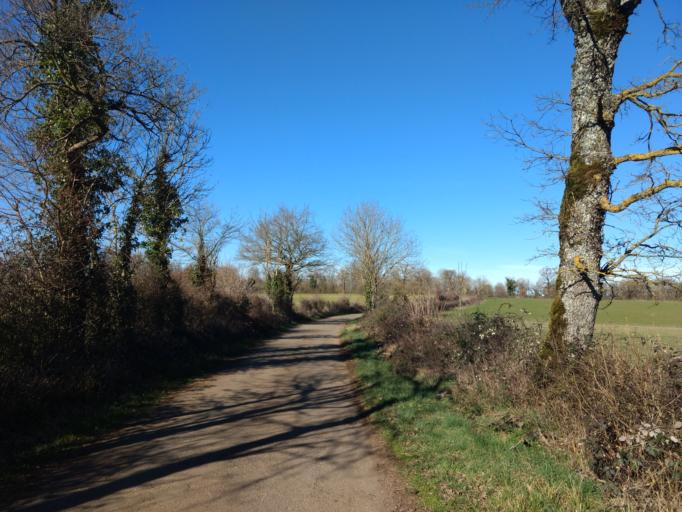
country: FR
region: Midi-Pyrenees
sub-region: Departement de l'Aveyron
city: Sebazac-Concoures
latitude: 44.4116
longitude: 2.5625
